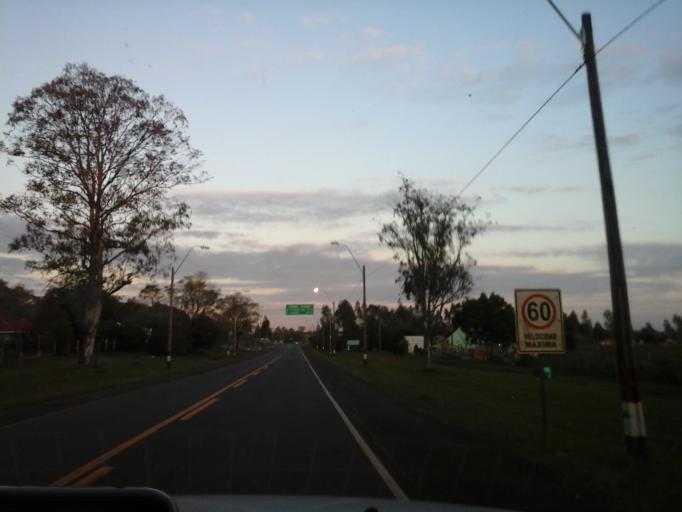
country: PY
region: Itapua
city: General Delgado
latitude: -27.0899
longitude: -56.5141
